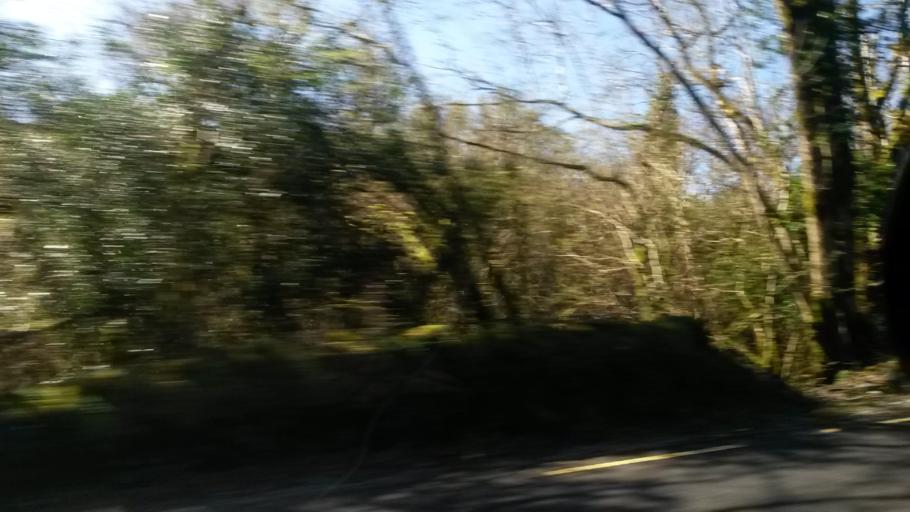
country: IE
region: Munster
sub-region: Ciarrai
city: Cill Airne
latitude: 51.9572
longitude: -9.3780
